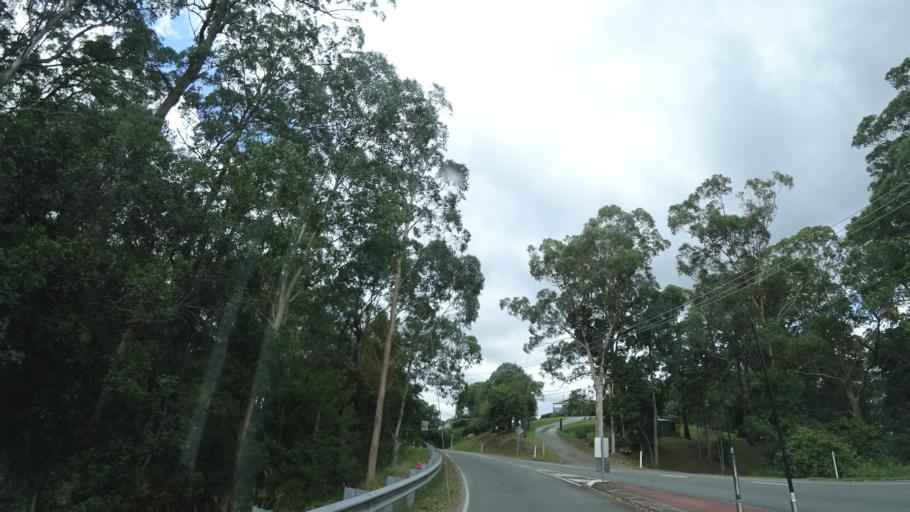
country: AU
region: Queensland
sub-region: Moreton Bay
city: Highvale
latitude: -27.3922
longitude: 152.7801
